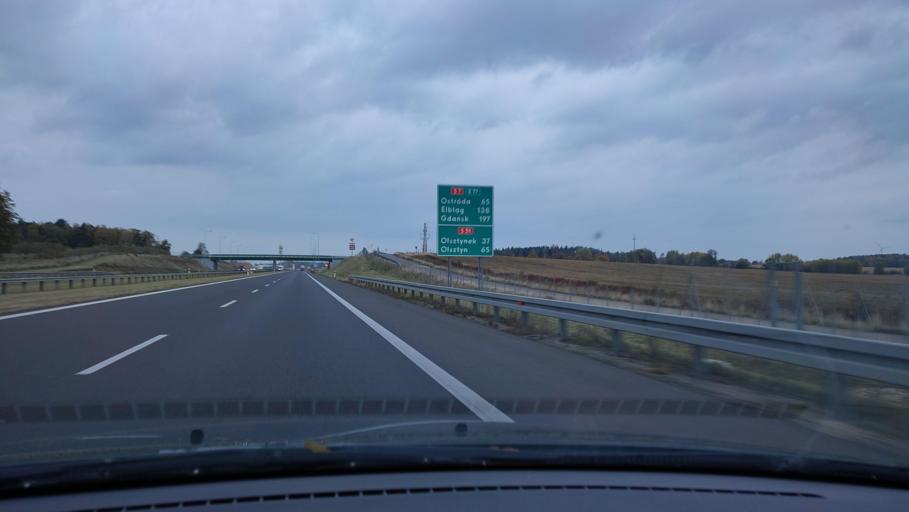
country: PL
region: Warmian-Masurian Voivodeship
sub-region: Powiat nidzicki
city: Nidzica
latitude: 53.2928
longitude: 20.4381
